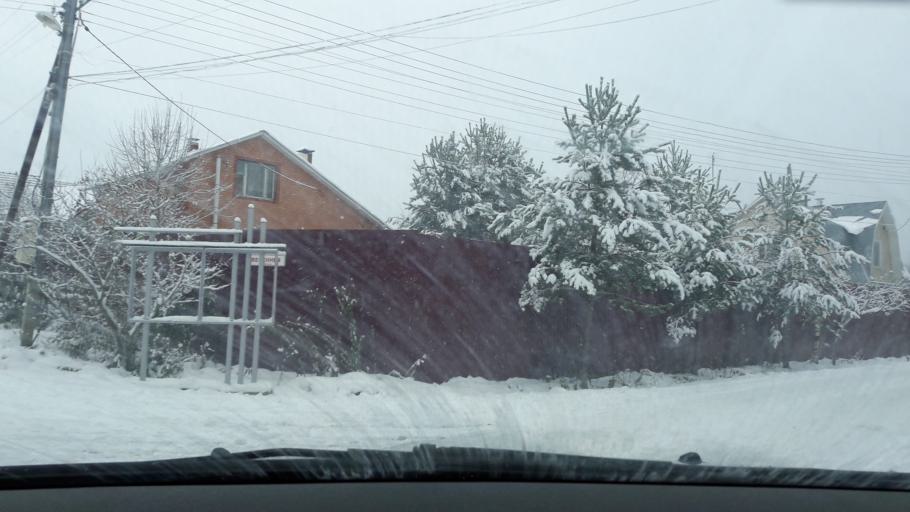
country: RU
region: Moskovskaya
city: Zvenigorod
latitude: 55.6417
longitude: 36.8118
